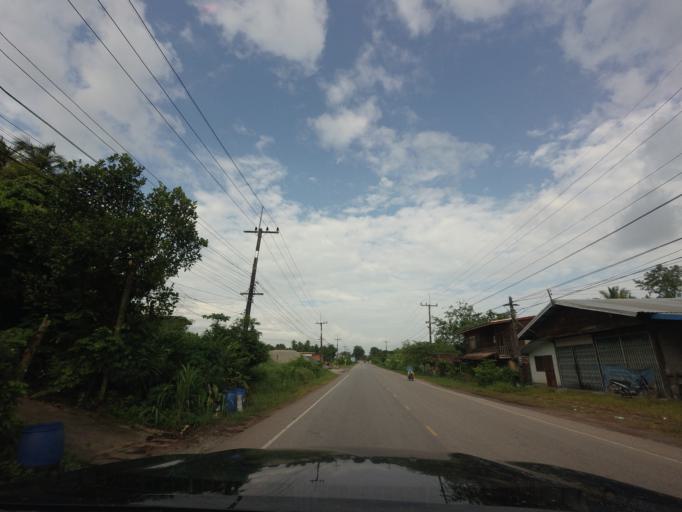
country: TH
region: Nong Khai
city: Pho Tak
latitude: 17.7797
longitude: 102.3891
